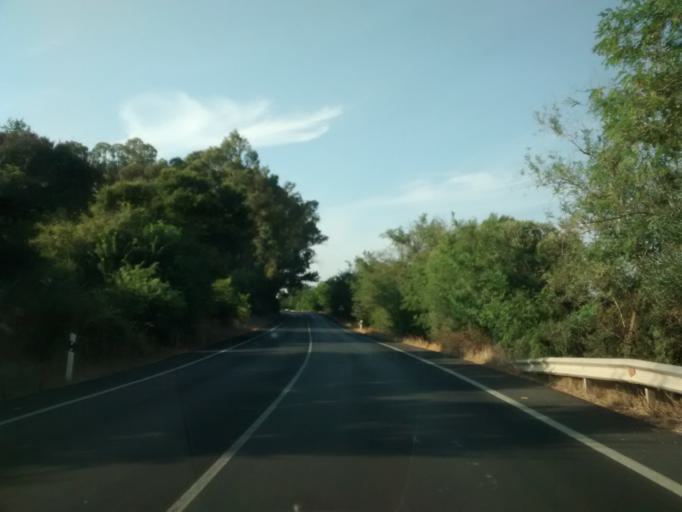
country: ES
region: Andalusia
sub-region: Provincia de Cadiz
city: Vejer de la Frontera
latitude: 36.2291
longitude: -5.9485
